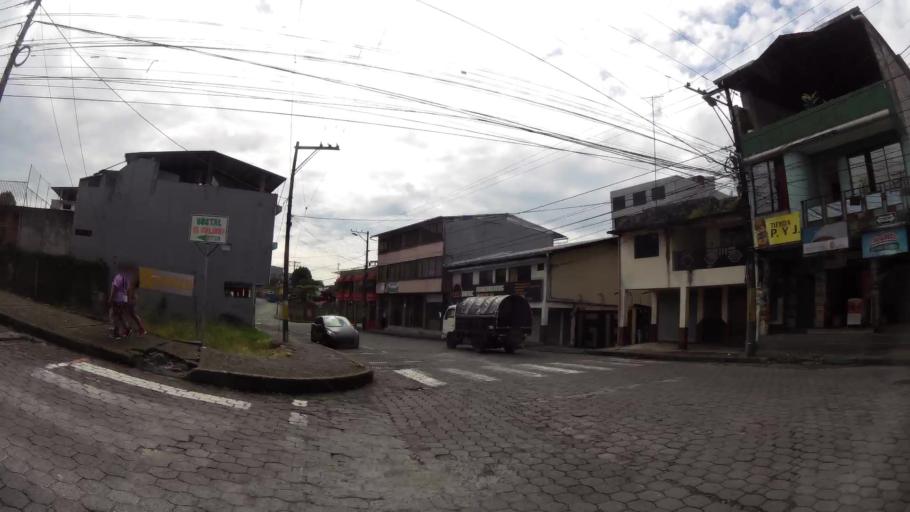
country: EC
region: Pastaza
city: Puyo
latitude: -1.4858
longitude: -78.0027
